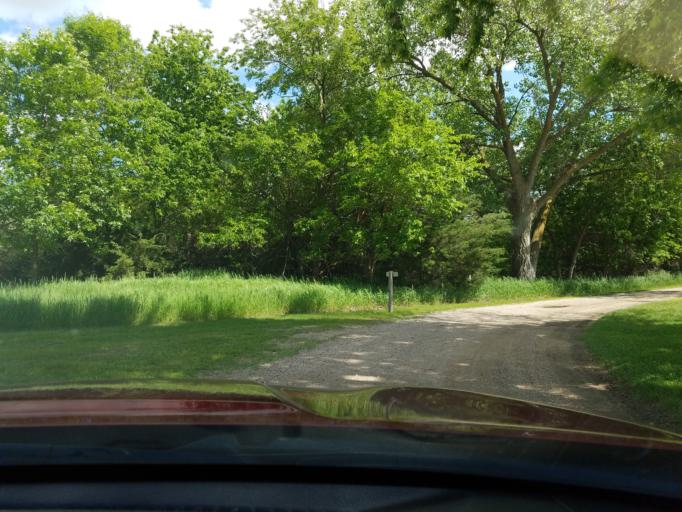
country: US
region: Nebraska
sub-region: Buffalo County
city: Kearney
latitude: 40.6562
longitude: -99.0087
